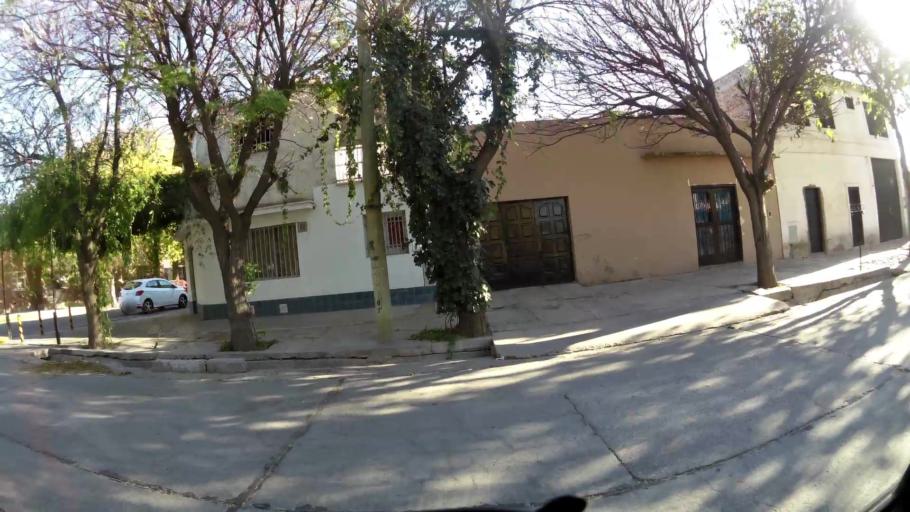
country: AR
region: Mendoza
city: Las Heras
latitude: -32.8586
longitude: -68.8302
